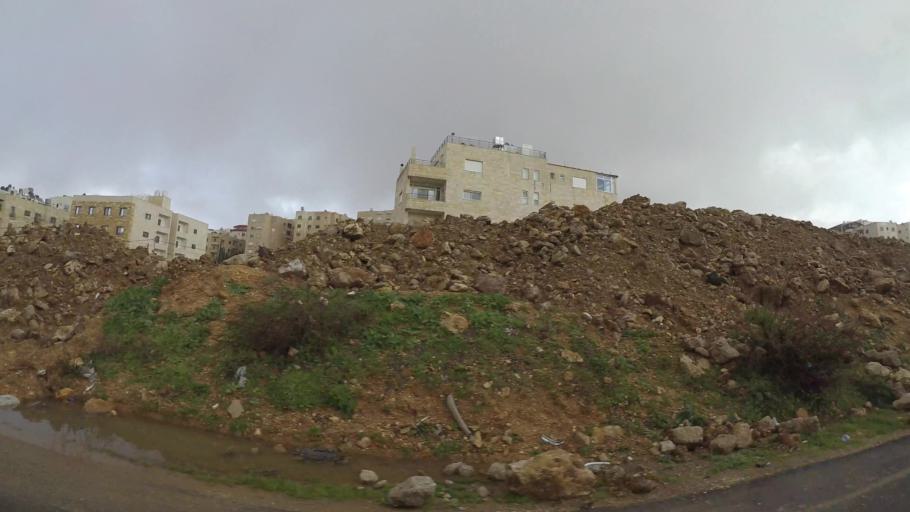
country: JO
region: Amman
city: Wadi as Sir
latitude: 31.9413
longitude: 35.8520
